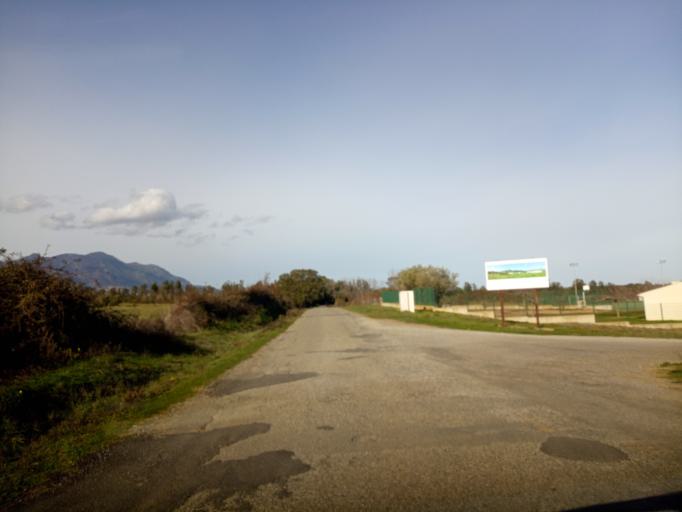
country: FR
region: Corsica
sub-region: Departement de la Haute-Corse
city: Linguizzetta
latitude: 42.2624
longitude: 9.5445
